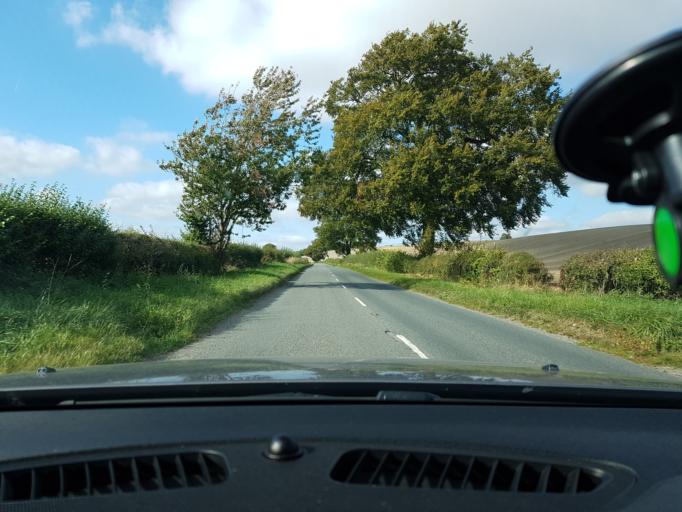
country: GB
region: England
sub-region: Wiltshire
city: Aldbourne
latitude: 51.4845
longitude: -1.6345
